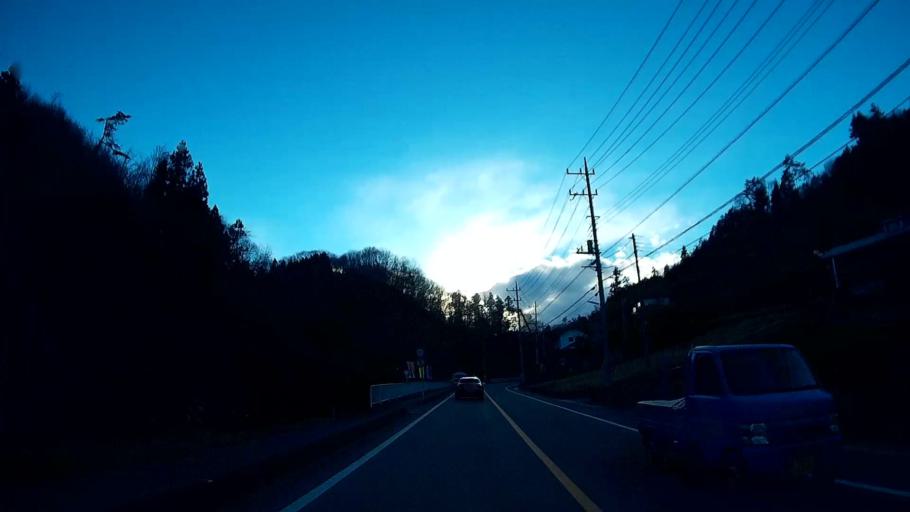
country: JP
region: Saitama
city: Chichibu
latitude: 36.0393
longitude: 138.9955
